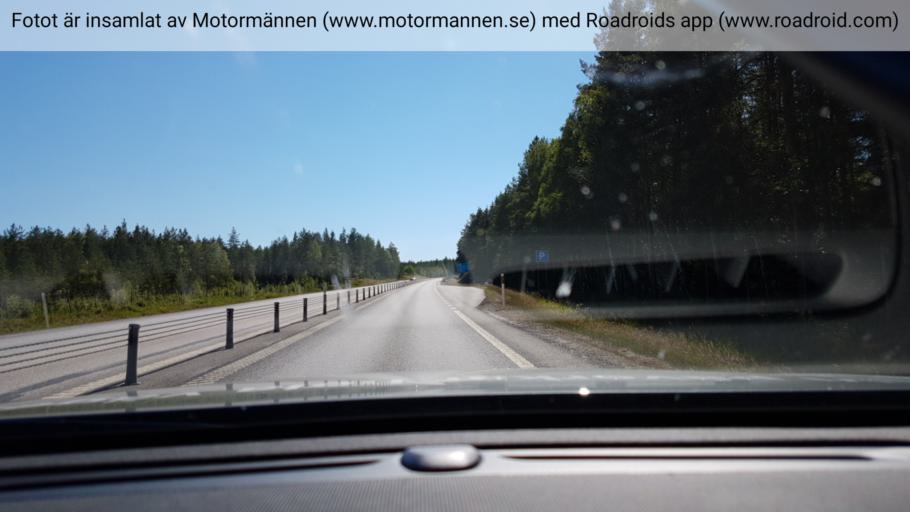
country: SE
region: Vaesterbotten
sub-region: Umea Kommun
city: Saevar
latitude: 63.9063
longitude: 20.5823
